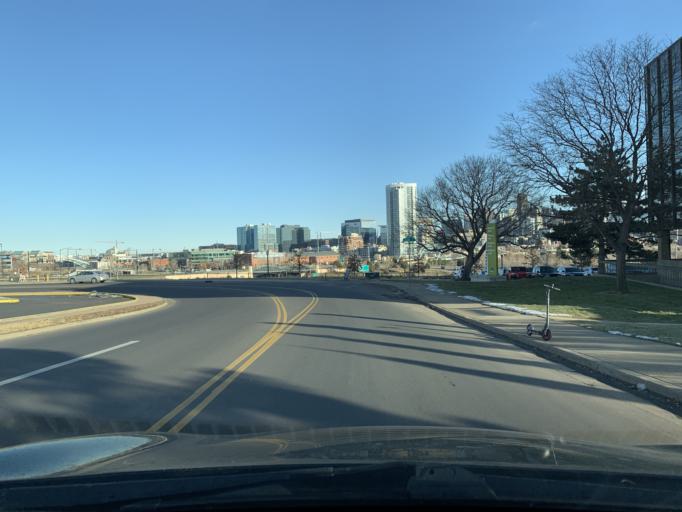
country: US
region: Colorado
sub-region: Denver County
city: Denver
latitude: 39.7548
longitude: -105.0165
